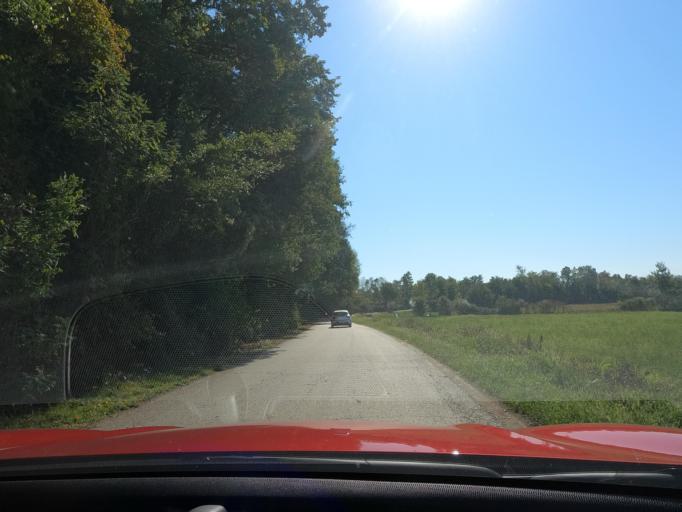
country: RS
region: Central Serbia
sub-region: Raski Okrug
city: Kraljevo
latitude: 43.7757
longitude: 20.6536
